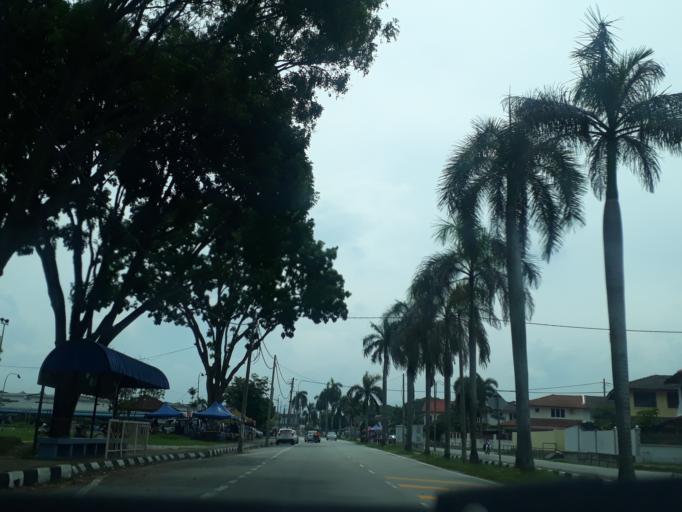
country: MY
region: Perak
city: Ipoh
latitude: 4.5941
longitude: 101.1298
